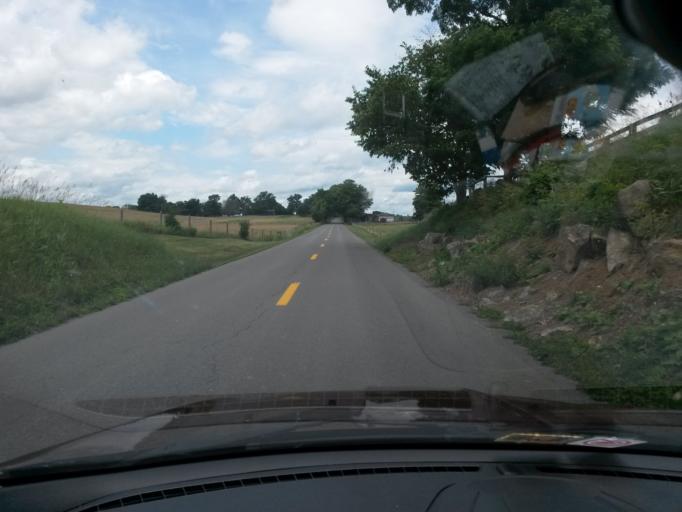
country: US
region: West Virginia
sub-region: Monroe County
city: Union
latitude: 37.5421
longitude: -80.5359
